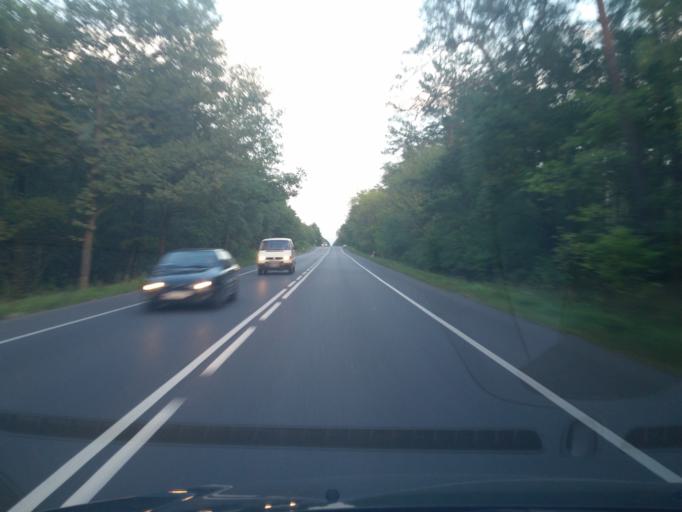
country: PL
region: Masovian Voivodeship
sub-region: Powiat warszawski zachodni
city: Kielpin
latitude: 52.3943
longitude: 20.8603
